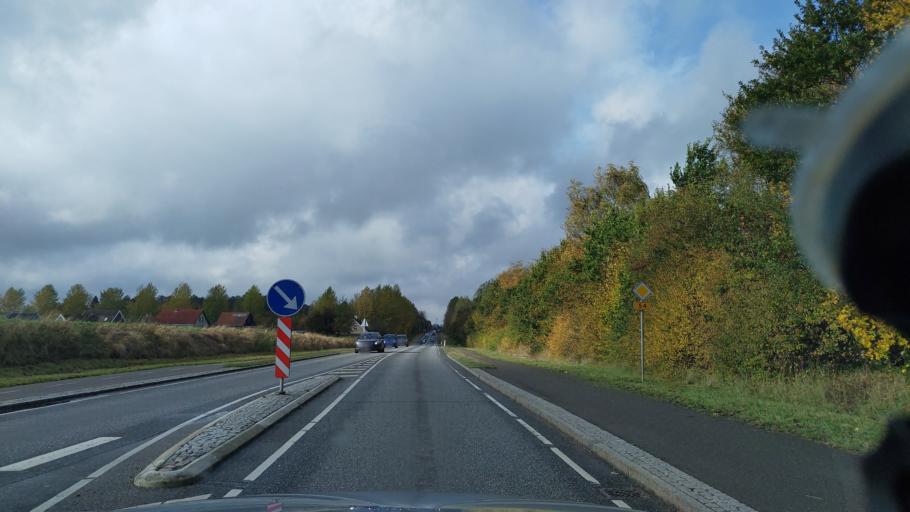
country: DK
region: Zealand
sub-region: Naestved Kommune
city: Fensmark
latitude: 55.2586
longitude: 11.8697
